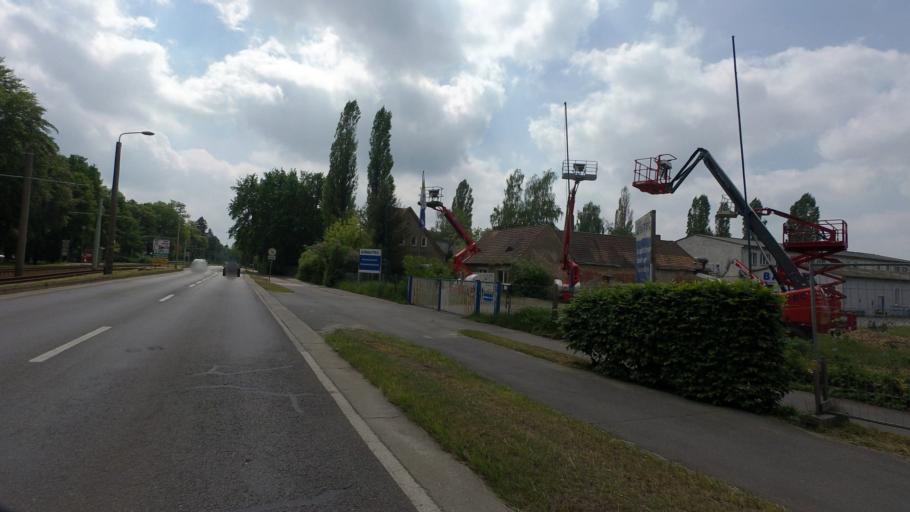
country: DE
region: Brandenburg
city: Cottbus
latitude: 51.7327
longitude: 14.3387
